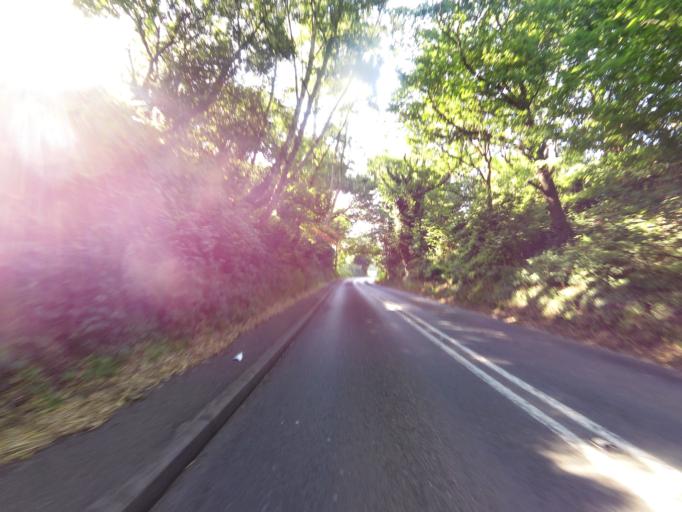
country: GB
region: England
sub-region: Suffolk
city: Woodbridge
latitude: 52.1000
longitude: 1.3472
